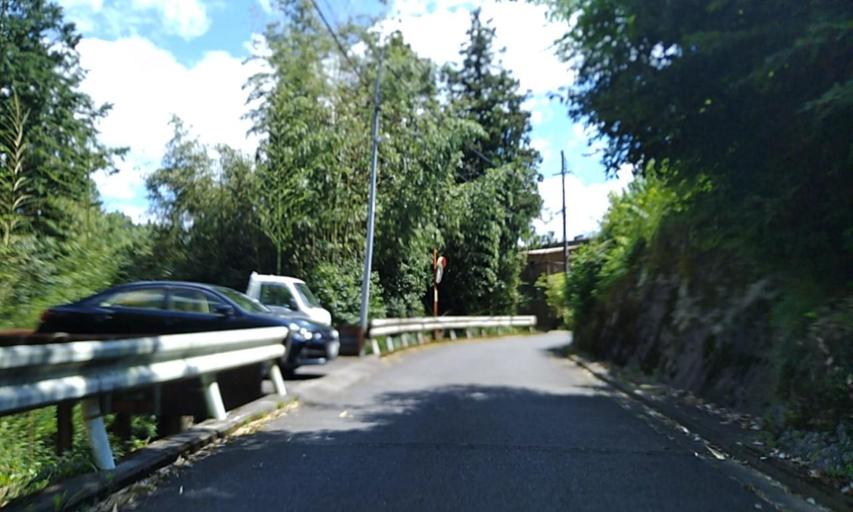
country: JP
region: Mie
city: Nabari
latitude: 34.7027
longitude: 136.0253
